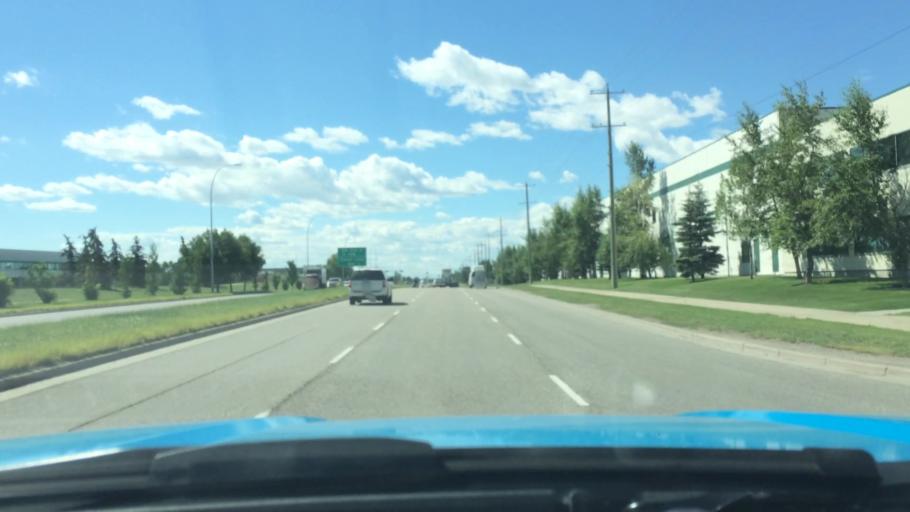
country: CA
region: Alberta
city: Calgary
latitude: 50.9968
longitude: -113.9587
